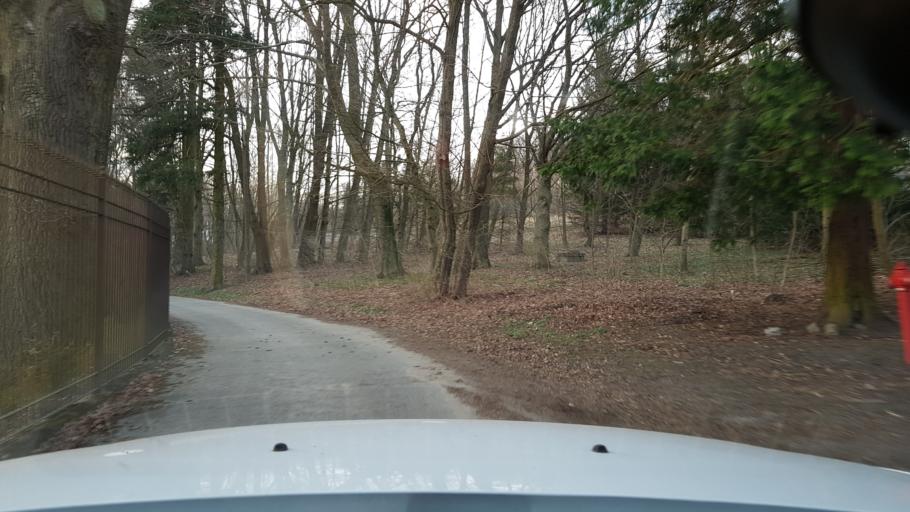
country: PL
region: West Pomeranian Voivodeship
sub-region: Koszalin
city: Koszalin
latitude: 54.1025
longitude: 16.1630
